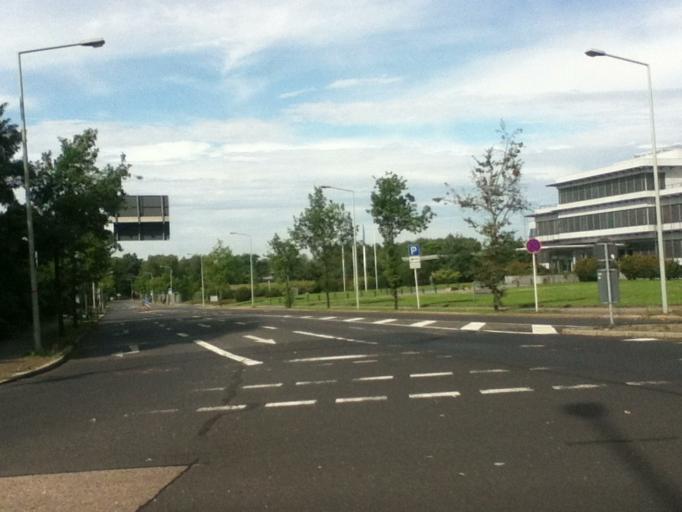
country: DE
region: Saxony
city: Albertstadt
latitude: 51.0996
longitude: 13.7357
